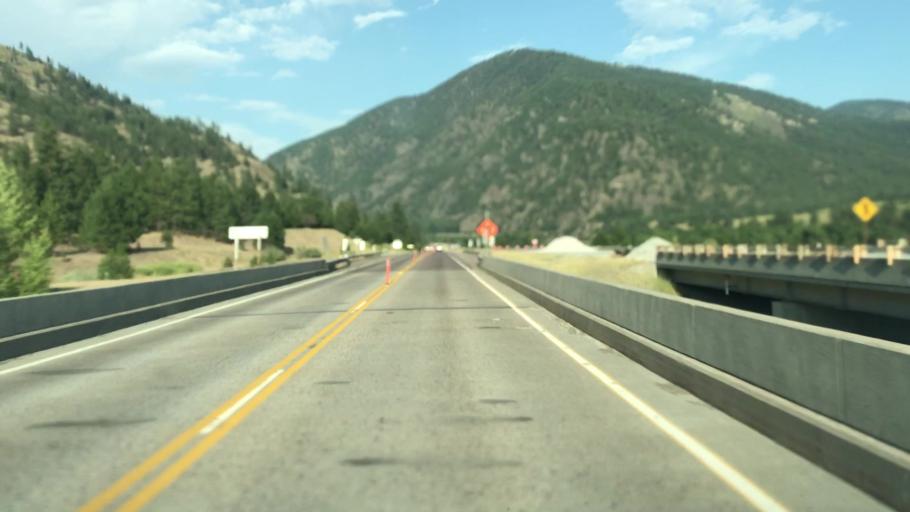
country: US
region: Montana
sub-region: Missoula County
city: Frenchtown
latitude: 47.0043
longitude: -114.5776
